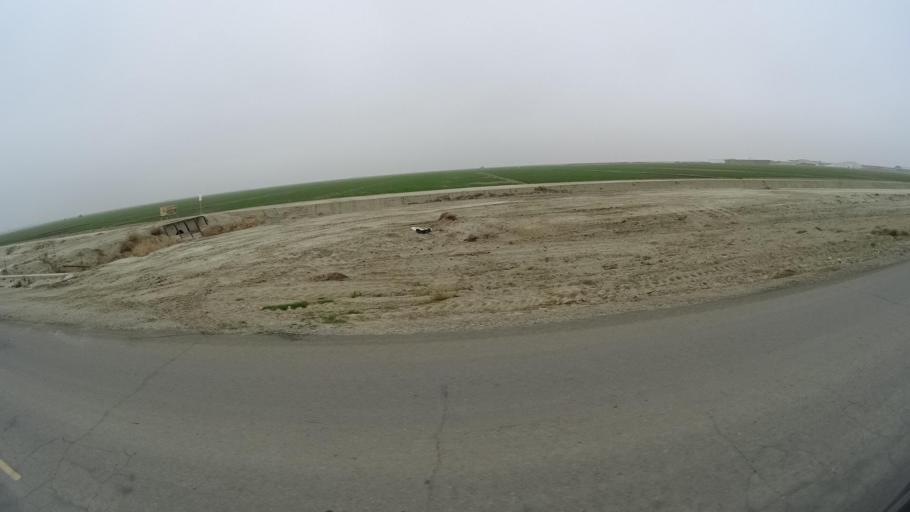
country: US
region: California
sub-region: Kern County
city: Rosedale
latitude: 35.2104
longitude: -119.2212
